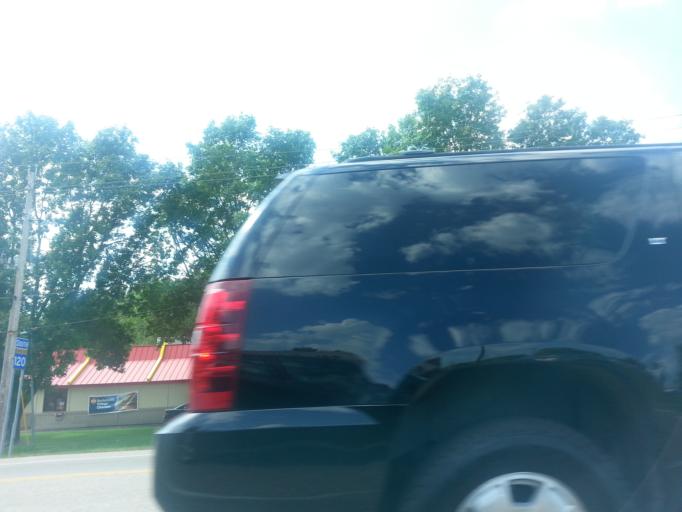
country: US
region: Minnesota
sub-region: Ramsey County
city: Maplewood
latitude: 44.9629
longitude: -92.9847
